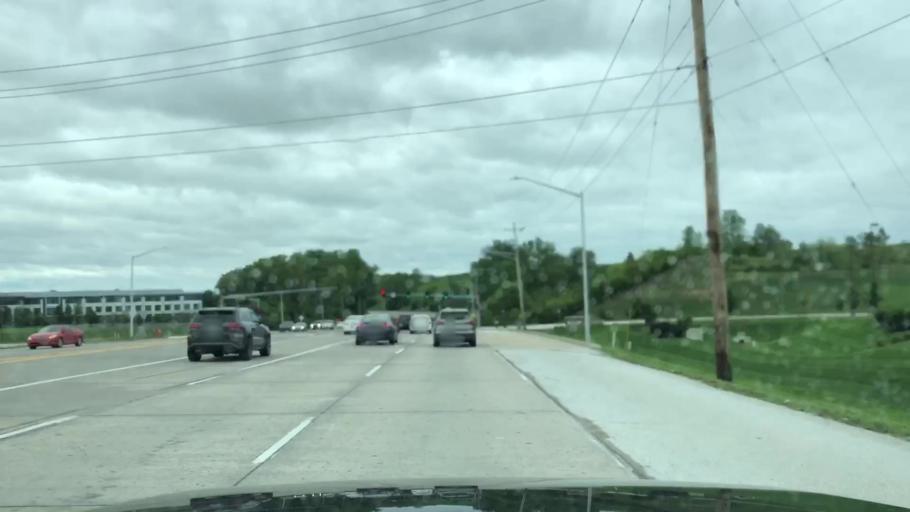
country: US
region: Missouri
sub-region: Saint Charles County
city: Saint Charles
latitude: 38.7433
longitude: -90.4681
